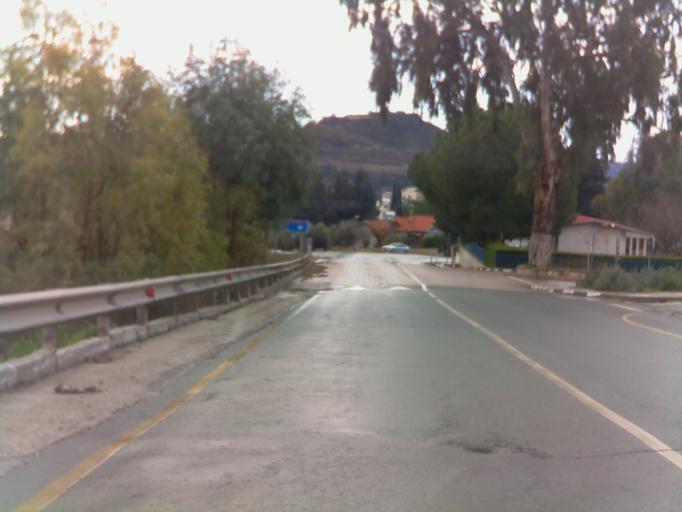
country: CY
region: Pafos
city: Tala
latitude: 34.8845
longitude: 32.4824
